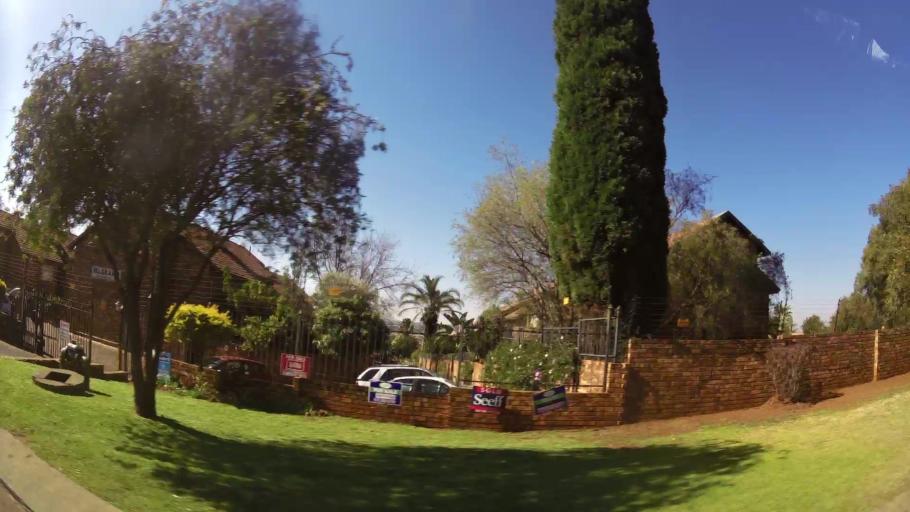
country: ZA
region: Gauteng
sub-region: City of Tshwane Metropolitan Municipality
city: Centurion
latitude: -25.8620
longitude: 28.1805
